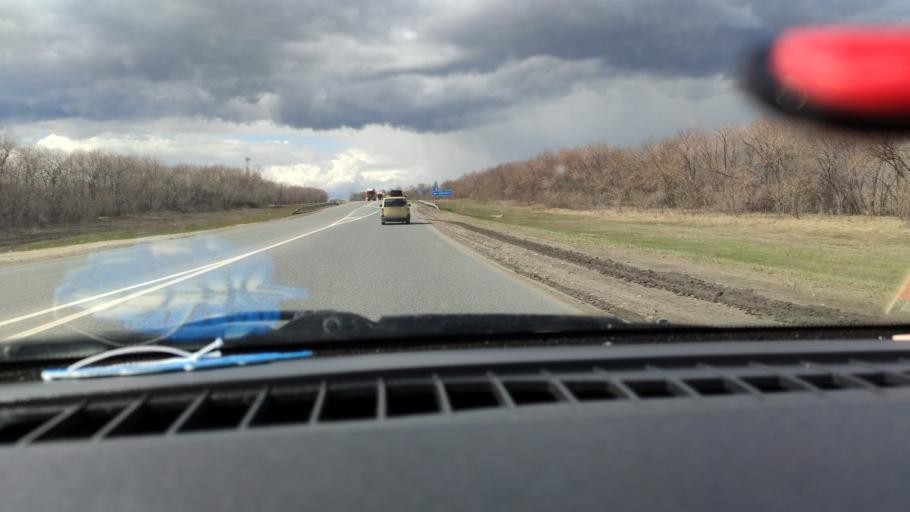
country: RU
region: Samara
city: Mezhdurechensk
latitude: 53.2559
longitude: 49.1347
